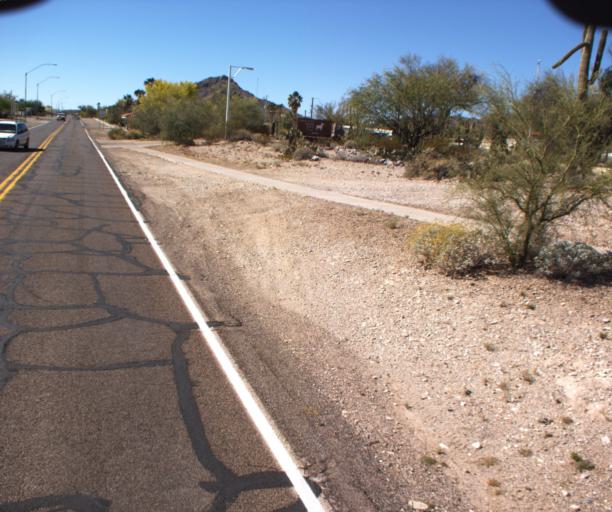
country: US
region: Arizona
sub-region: Pima County
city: Ajo
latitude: 32.3867
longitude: -112.8723
